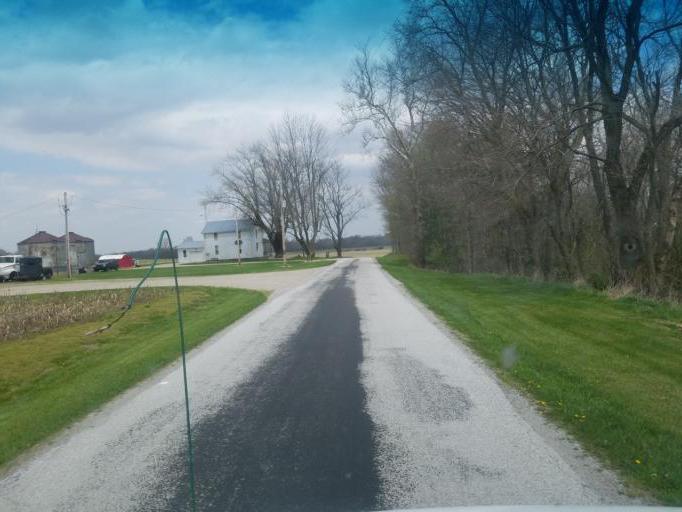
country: US
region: Ohio
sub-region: Wyandot County
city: Upper Sandusky
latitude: 40.9195
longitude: -83.2549
